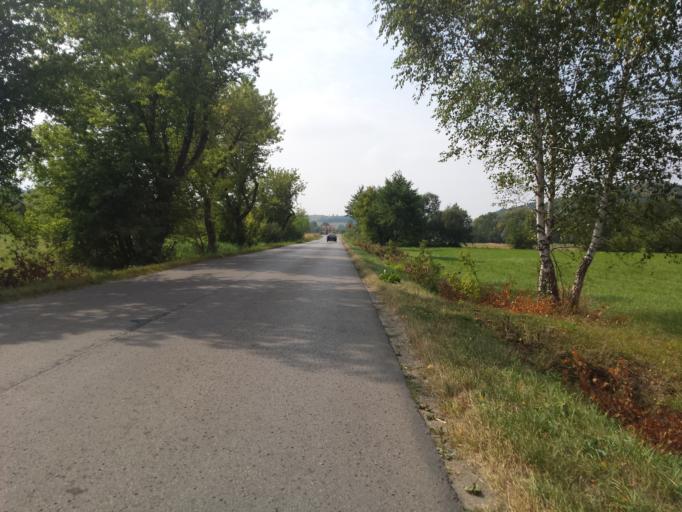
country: PL
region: Subcarpathian Voivodeship
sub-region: Powiat rzeszowski
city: Blazowa
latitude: 49.8748
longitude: 22.1175
